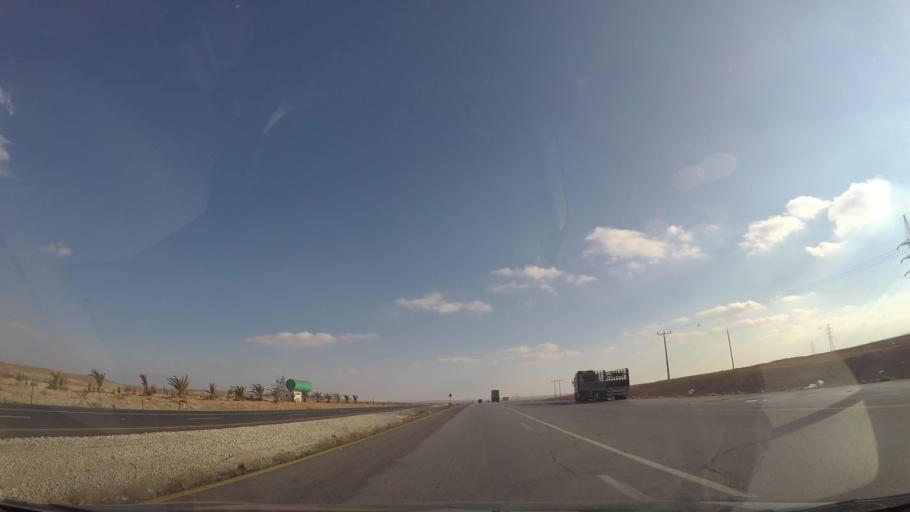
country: JO
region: Karak
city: Karak City
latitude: 31.1419
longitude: 36.0264
